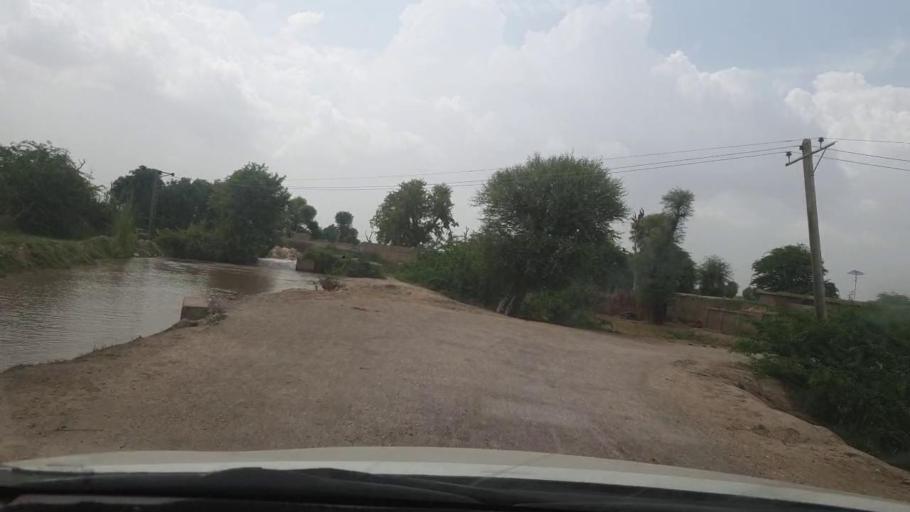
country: PK
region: Sindh
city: Kot Diji
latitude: 27.3076
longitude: 69.0131
